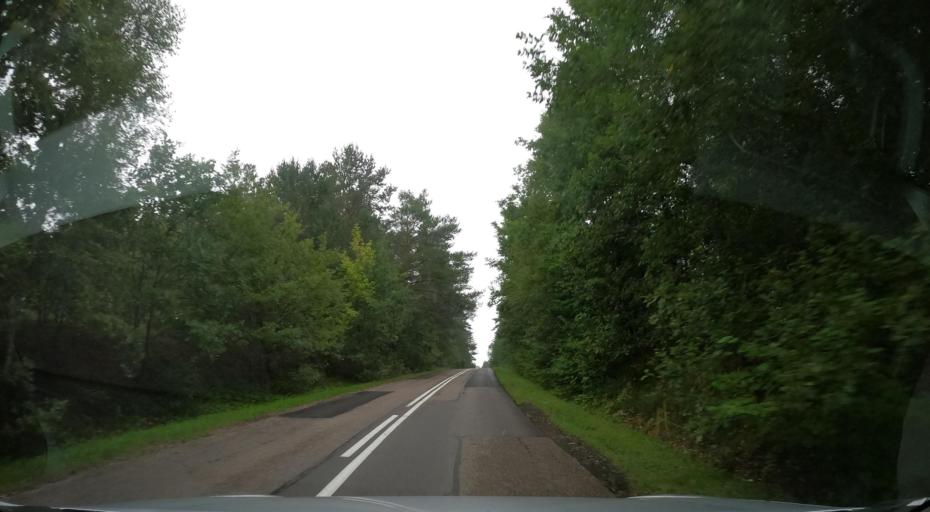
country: PL
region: Pomeranian Voivodeship
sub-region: Powiat wejherowski
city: Linia
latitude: 54.4654
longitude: 17.9846
